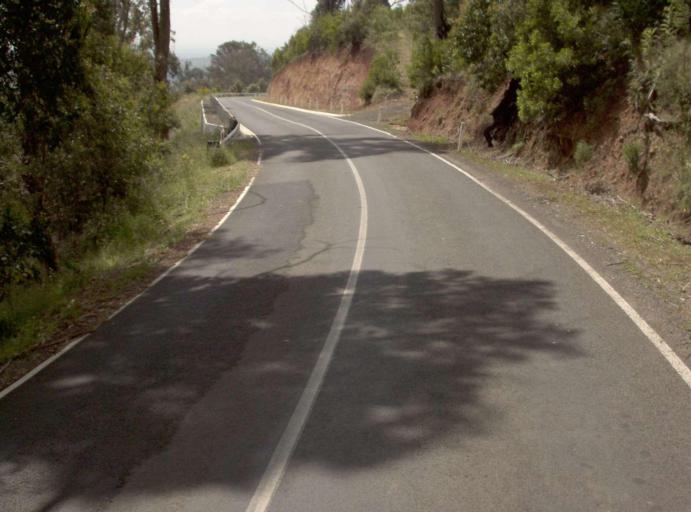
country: AU
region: Victoria
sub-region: Latrobe
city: Traralgon
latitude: -38.3333
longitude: 146.5724
